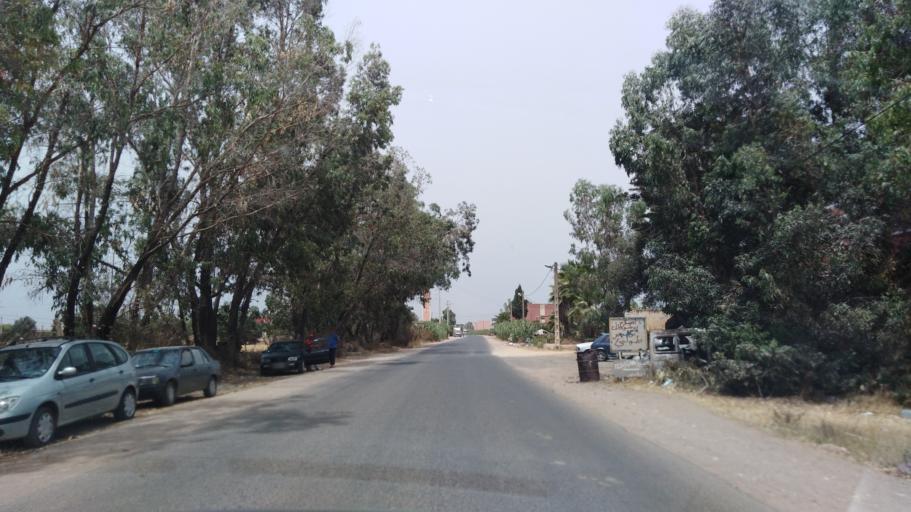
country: MA
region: Grand Casablanca
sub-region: Mediouna
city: Mediouna
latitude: 33.3980
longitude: -7.5112
